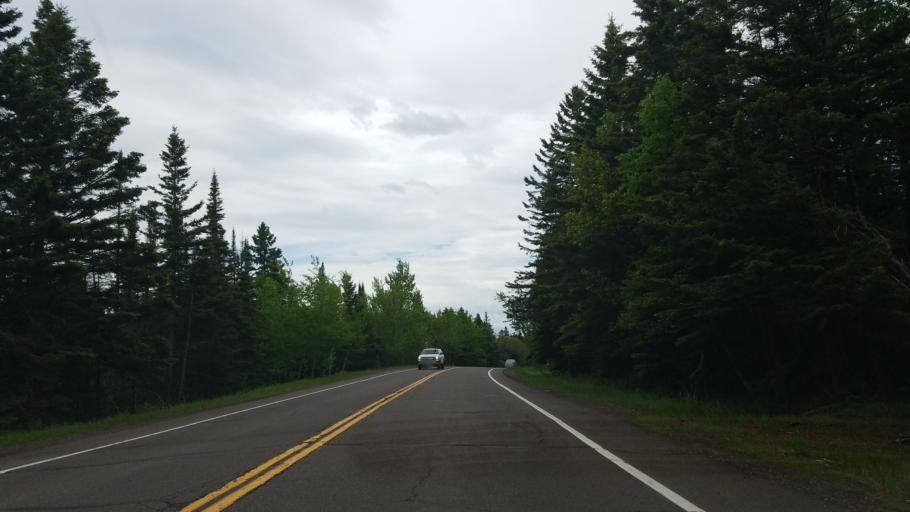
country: US
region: Minnesota
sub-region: Lake County
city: Two Harbors
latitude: 47.0529
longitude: -91.6224
